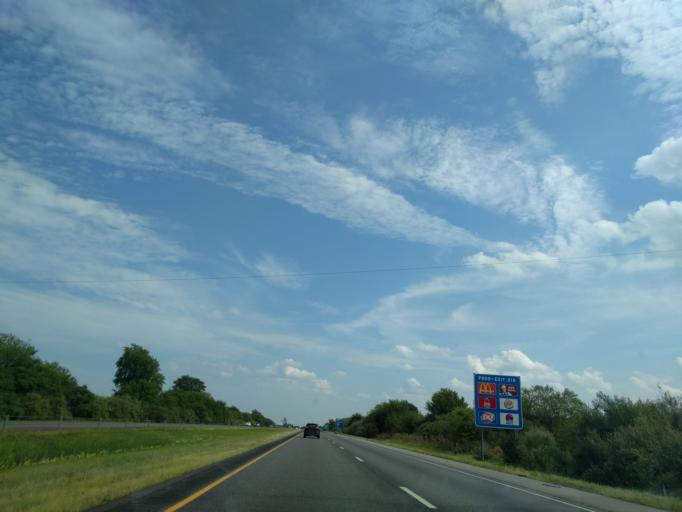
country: US
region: Indiana
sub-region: Jasper County
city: Rensselaer
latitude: 40.9628
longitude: -87.2366
